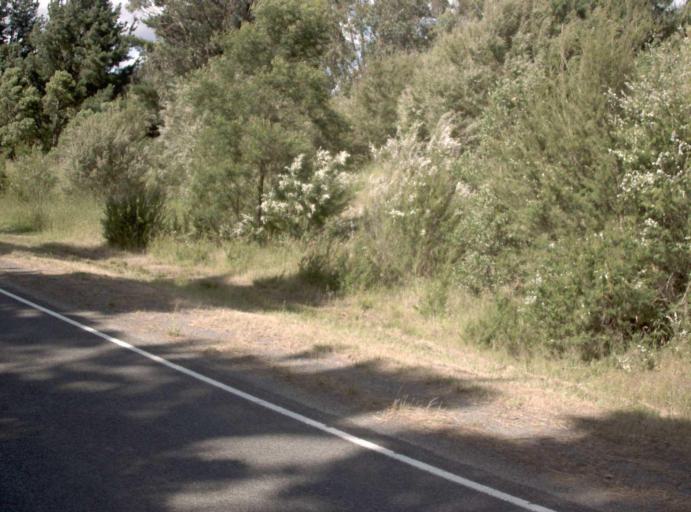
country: AU
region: Victoria
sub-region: Latrobe
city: Morwell
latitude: -38.1864
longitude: 146.4046
